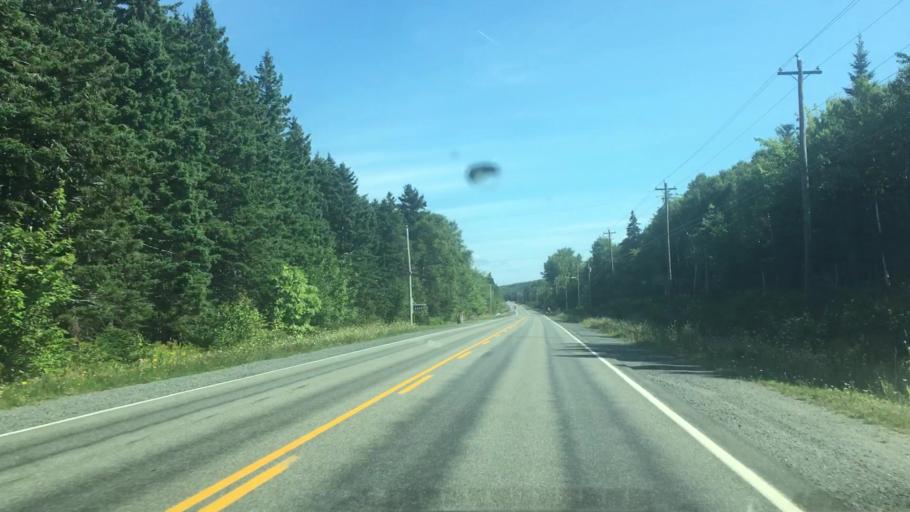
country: CA
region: Nova Scotia
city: Sydney
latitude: 45.9819
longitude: -60.4252
